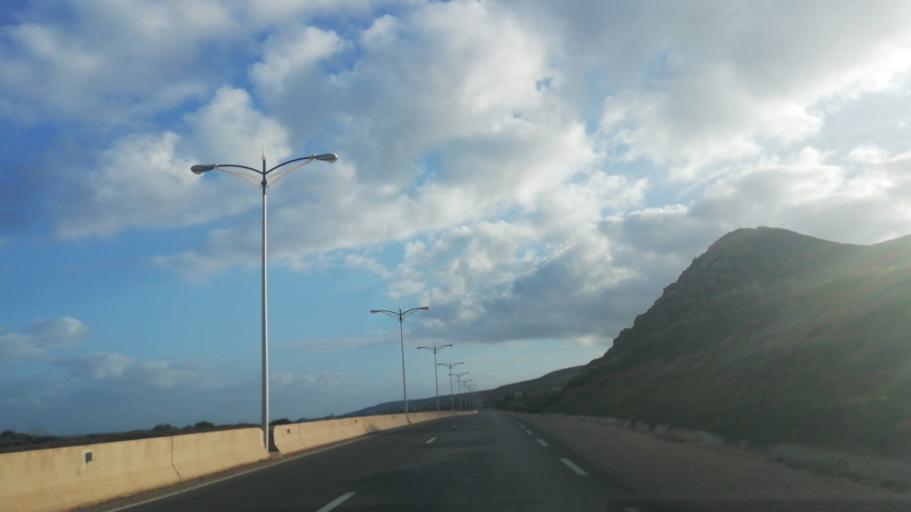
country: DZ
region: Mostaganem
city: Mostaganem
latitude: 36.0538
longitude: 0.1569
